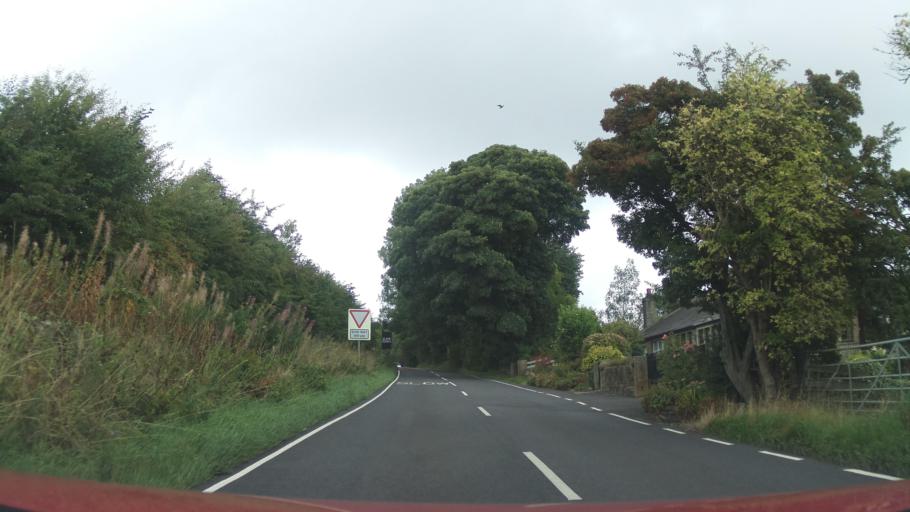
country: GB
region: England
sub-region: Kirklees
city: Shelley
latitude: 53.5766
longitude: -1.7057
